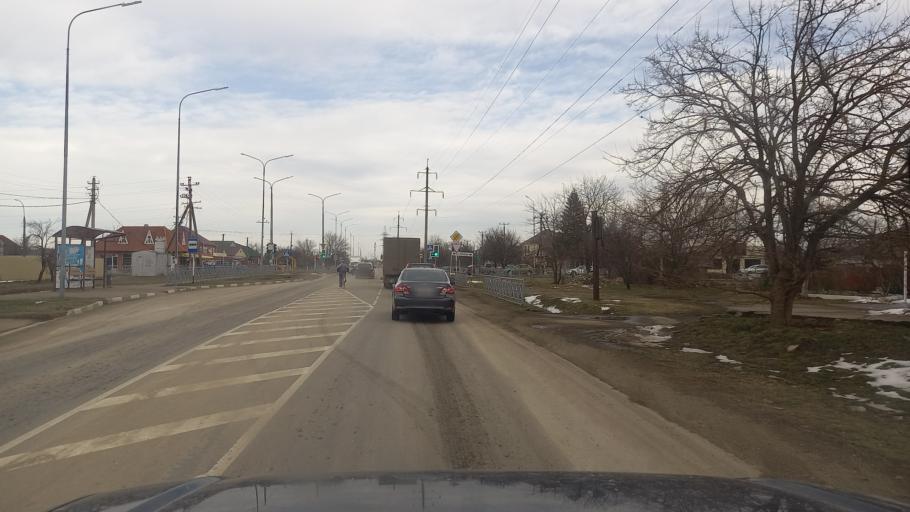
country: RU
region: Krasnodarskiy
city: Belorechensk
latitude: 44.7582
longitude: 39.8830
